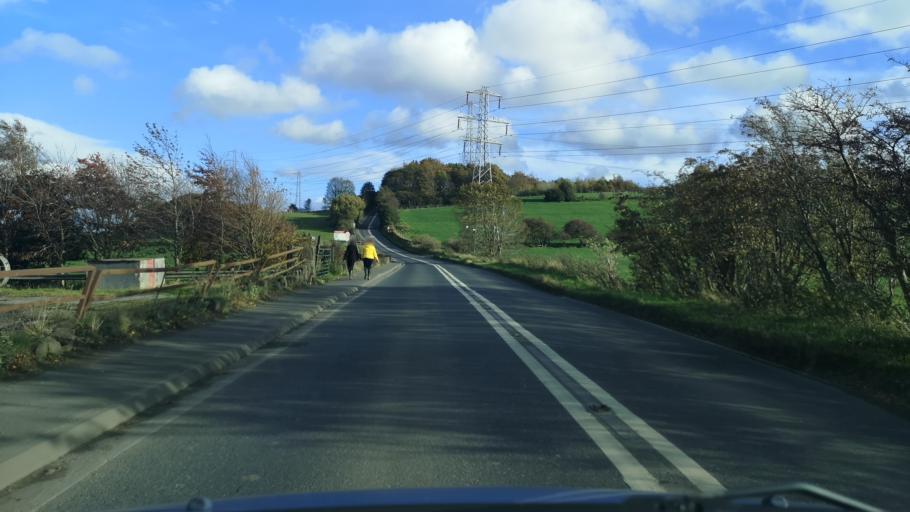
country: GB
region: England
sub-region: Kirklees
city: Mirfield
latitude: 53.6514
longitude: -1.6902
